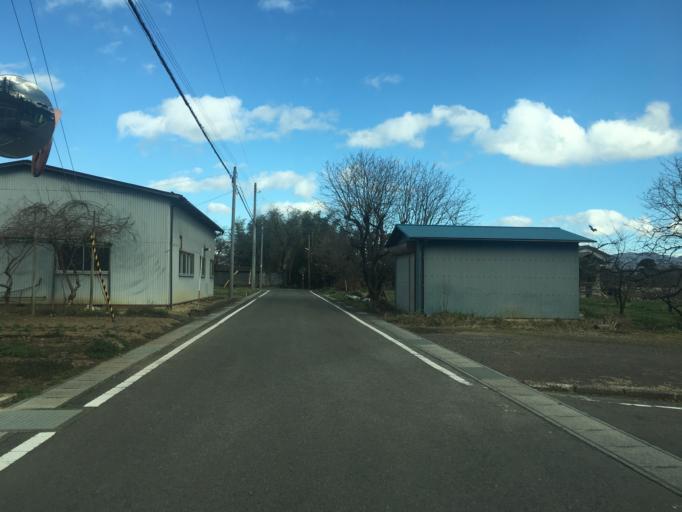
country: JP
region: Fukushima
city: Yanagawamachi-saiwaicho
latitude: 37.8868
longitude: 140.5794
